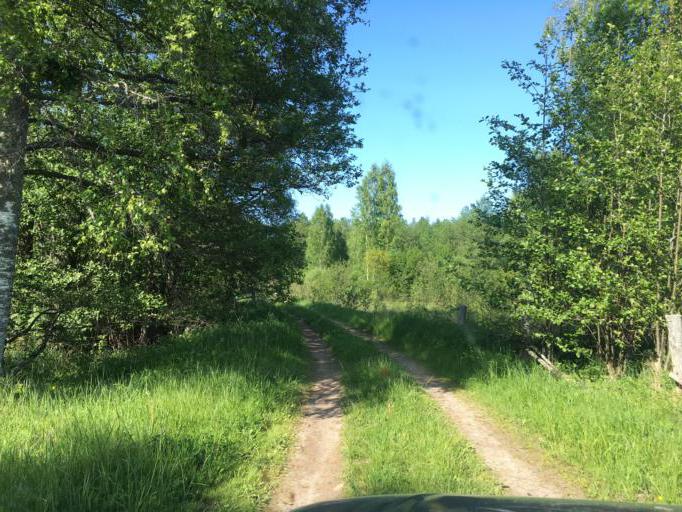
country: LV
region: Dundaga
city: Dundaga
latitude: 57.6003
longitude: 22.5068
